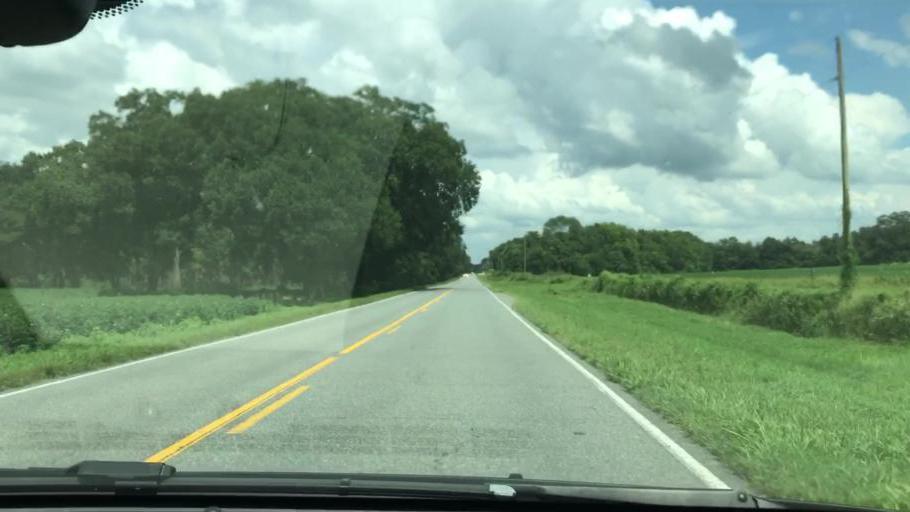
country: US
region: Florida
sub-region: Jackson County
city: Malone
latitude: 30.8991
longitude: -85.1365
